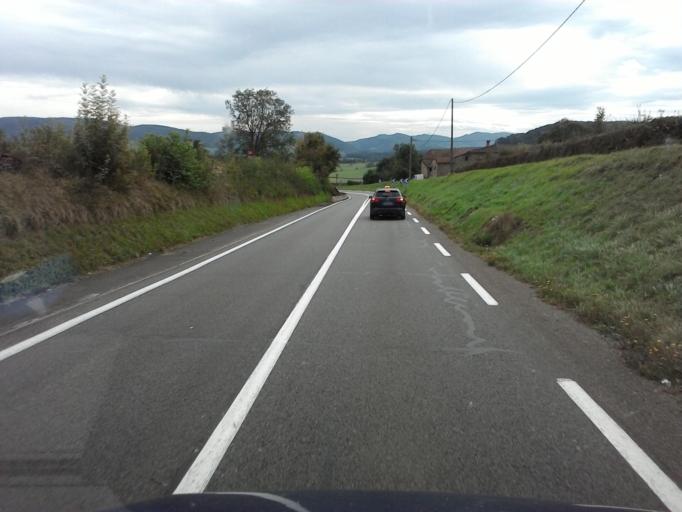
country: FR
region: Bourgogne
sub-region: Departement de Saone-et-Loire
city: Cluny
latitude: 46.4432
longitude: 4.6396
